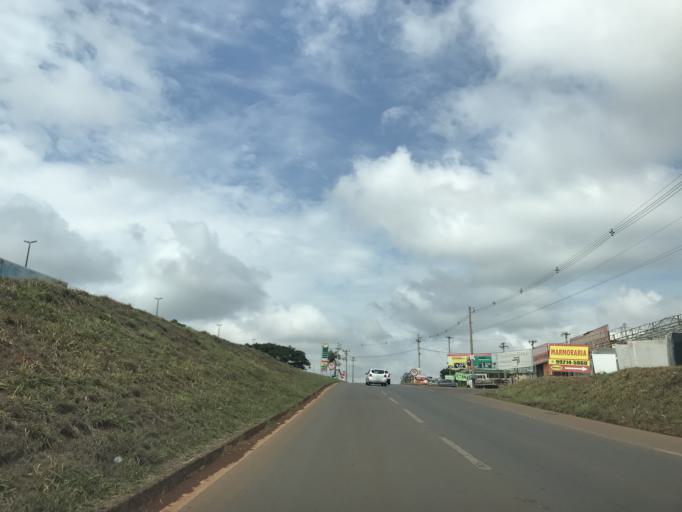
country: BR
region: Federal District
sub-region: Brasilia
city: Brasilia
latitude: -15.6814
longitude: -47.8380
